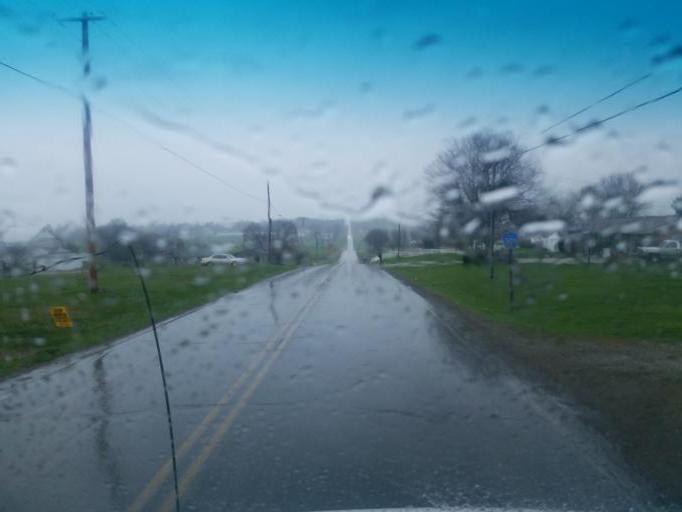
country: US
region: Ohio
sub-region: Wayne County
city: Apple Creek
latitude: 40.6891
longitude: -81.8783
